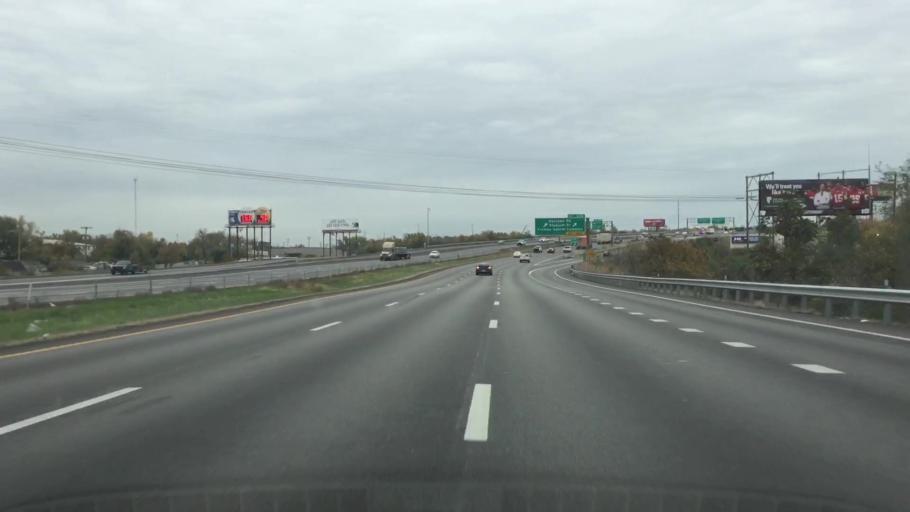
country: US
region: Missouri
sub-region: Jackson County
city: Raytown
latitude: 39.0475
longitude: -94.4995
